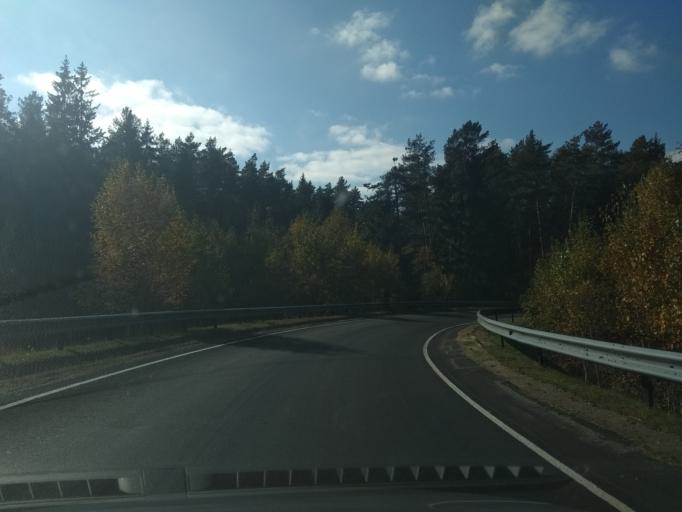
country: BY
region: Brest
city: Baranovichi
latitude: 53.0470
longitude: 25.8449
